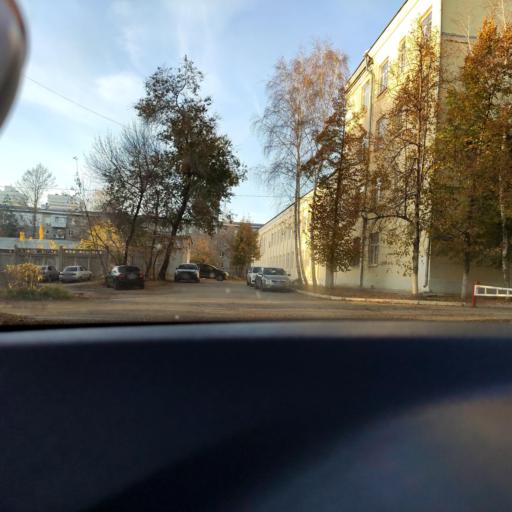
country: RU
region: Samara
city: Samara
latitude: 53.1990
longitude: 50.1605
